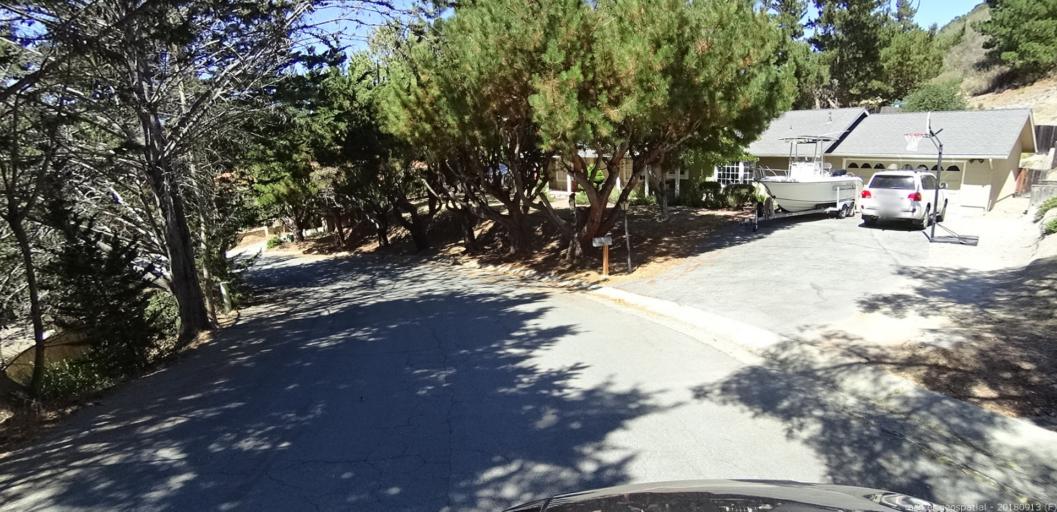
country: US
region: California
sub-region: Monterey County
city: Carmel Valley Village
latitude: 36.5426
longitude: -121.7975
